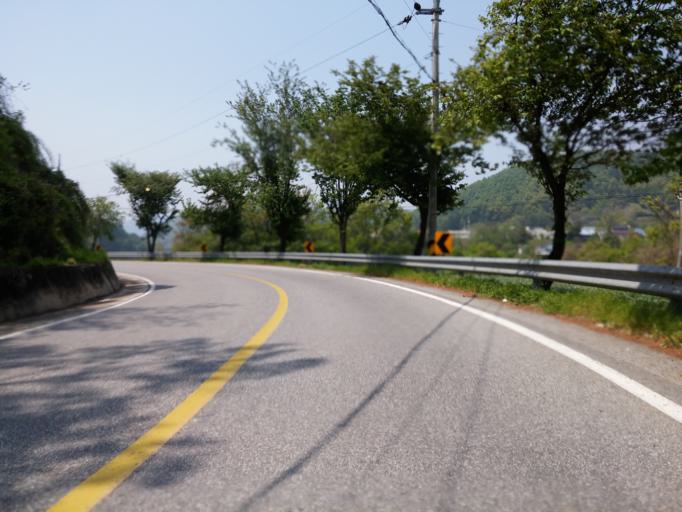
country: KR
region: Chungcheongbuk-do
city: Okcheon
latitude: 36.4440
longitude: 127.5845
